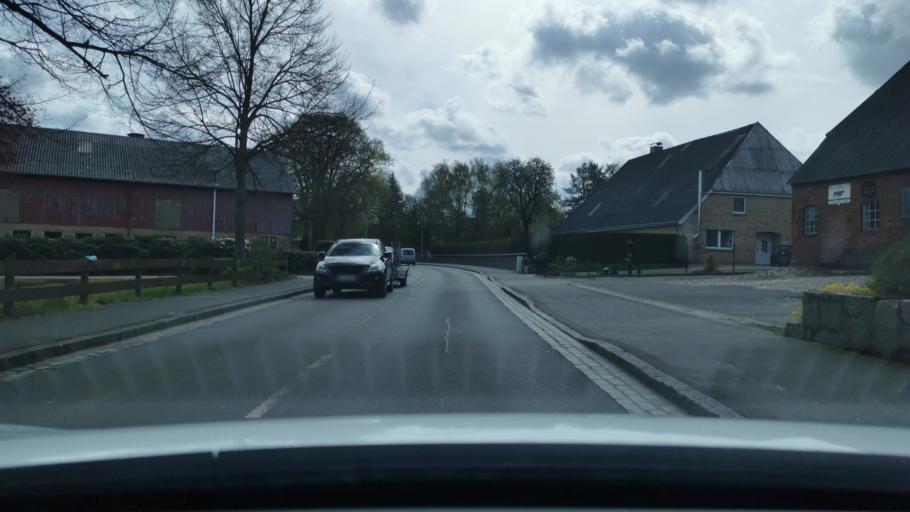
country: DE
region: Schleswig-Holstein
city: Hamdorf
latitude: 54.2264
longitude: 9.5152
